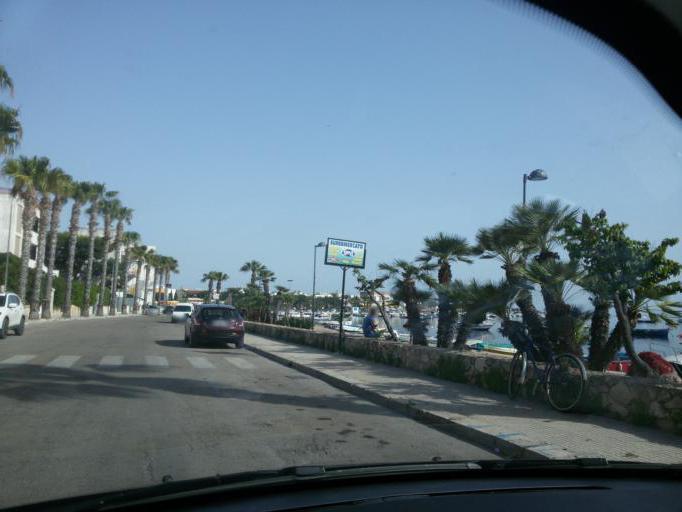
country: IT
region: Apulia
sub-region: Provincia di Lecce
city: Porto Cesareo
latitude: 40.2613
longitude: 17.8897
